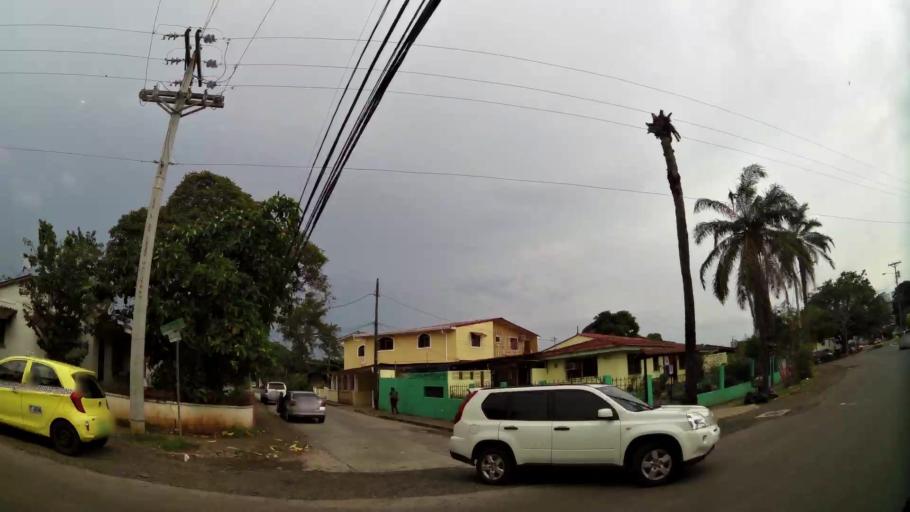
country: PA
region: Panama
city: Panama
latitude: 9.0042
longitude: -79.5246
